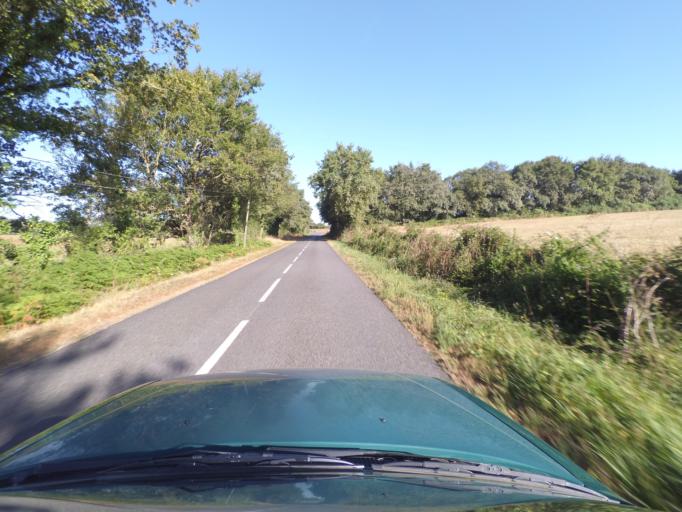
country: FR
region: Pays de la Loire
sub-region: Departement de la Loire-Atlantique
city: Le Bignon
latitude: 47.1148
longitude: -1.5203
